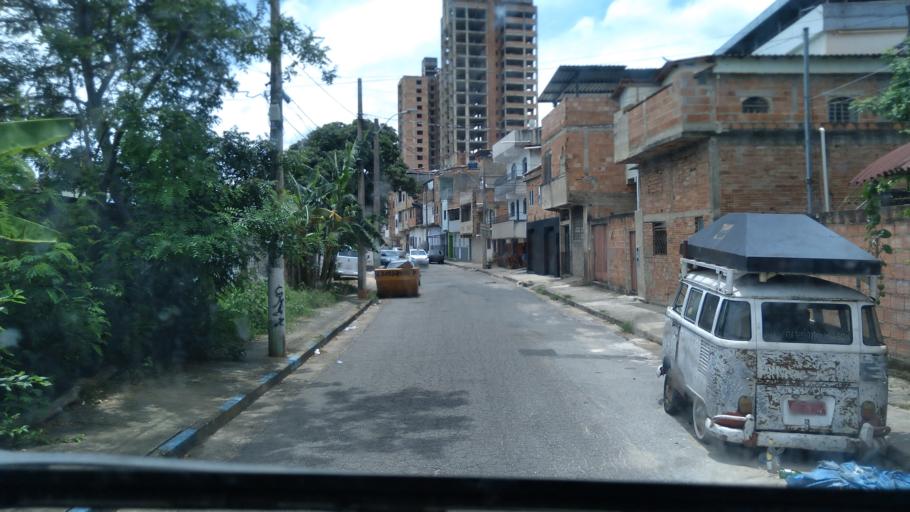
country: BR
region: Minas Gerais
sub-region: Belo Horizonte
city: Belo Horizonte
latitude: -19.9178
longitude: -43.9201
